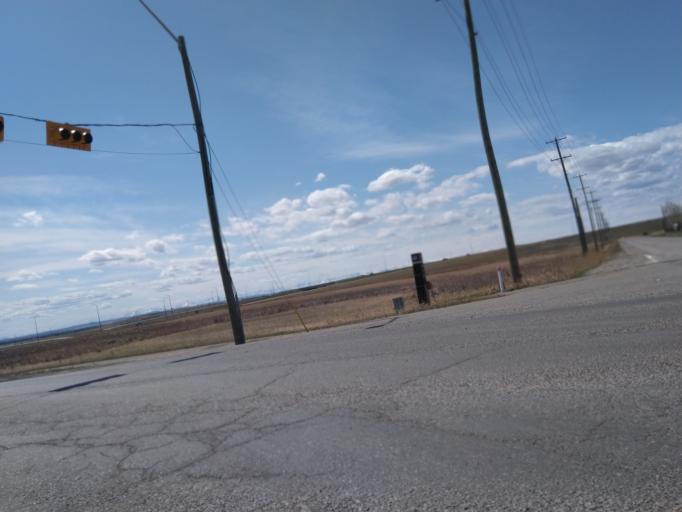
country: CA
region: Alberta
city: Chestermere
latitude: 50.9505
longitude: -113.9118
